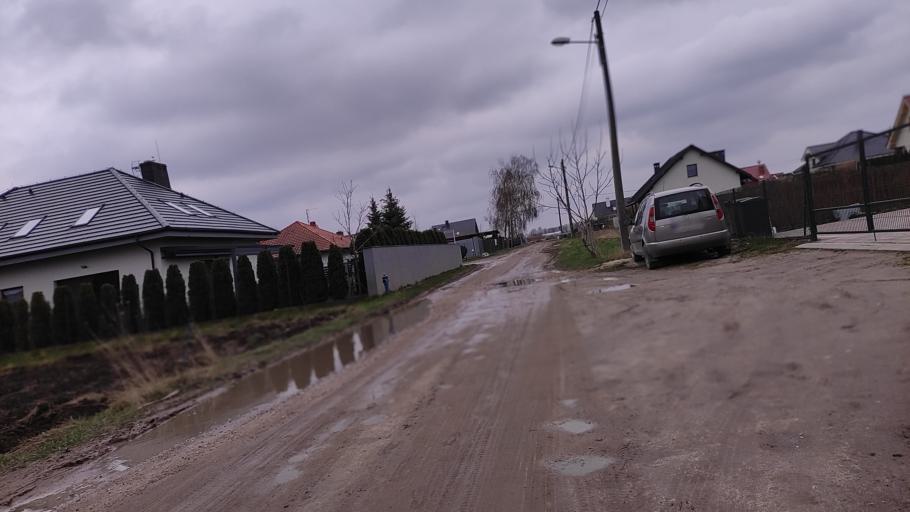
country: PL
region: Greater Poland Voivodeship
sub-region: Powiat poznanski
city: Kostrzyn
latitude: 52.4026
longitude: 17.1727
